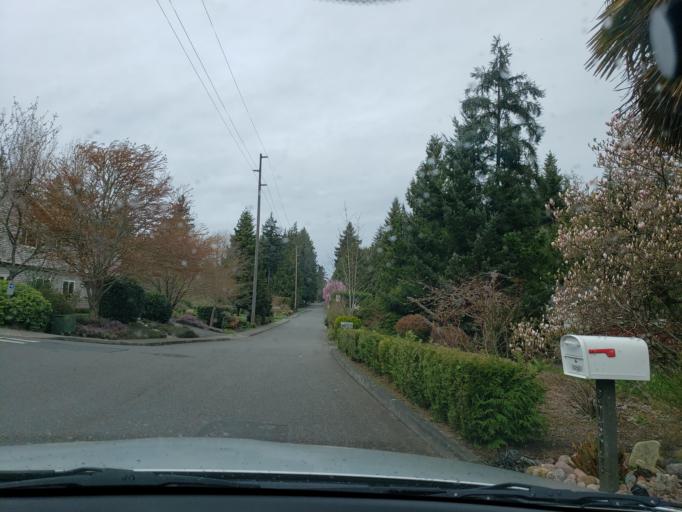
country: US
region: Washington
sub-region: Snohomish County
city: Esperance
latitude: 47.8126
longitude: -122.3520
